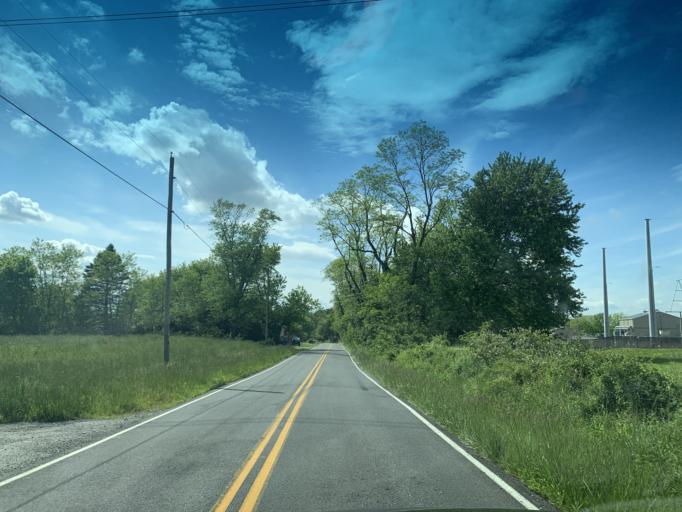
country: US
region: Maryland
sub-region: Cecil County
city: Rising Sun
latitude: 39.7169
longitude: -76.1623
